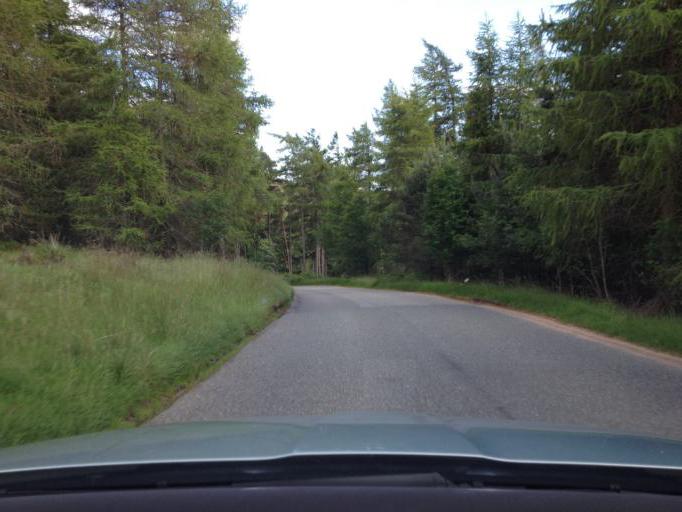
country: GB
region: Scotland
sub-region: Aberdeenshire
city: Banchory
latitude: 56.9518
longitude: -2.5852
